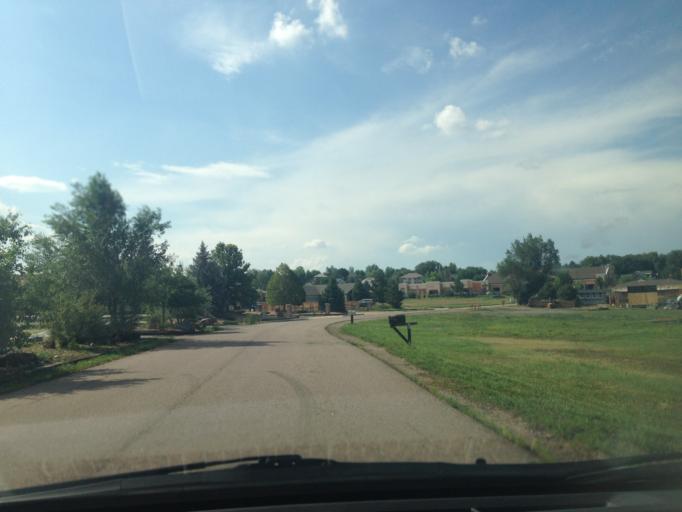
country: US
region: Colorado
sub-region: Broomfield County
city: Broomfield
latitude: 39.8903
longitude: -105.0818
